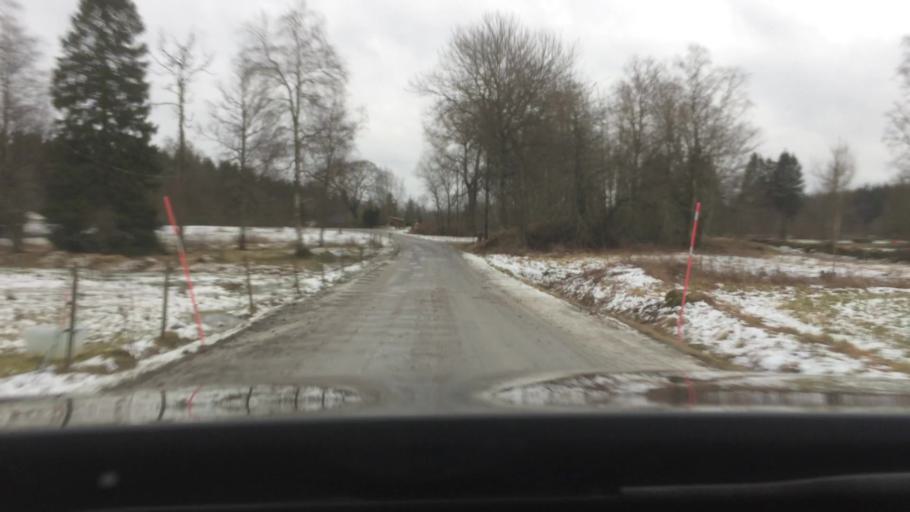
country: SE
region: Vaestra Goetaland
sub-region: Falkopings Kommun
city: Floby
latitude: 57.9908
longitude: 13.4056
